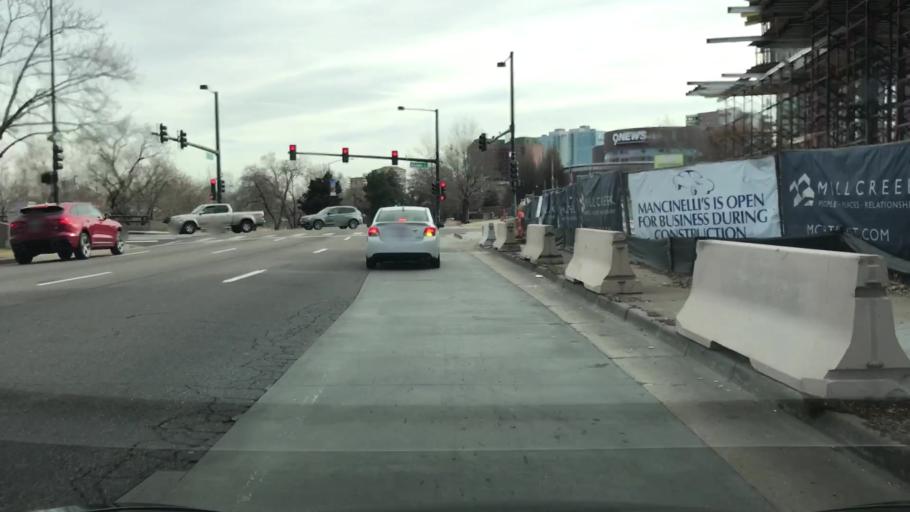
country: US
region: Colorado
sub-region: Denver County
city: Denver
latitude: 39.7229
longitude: -104.9832
